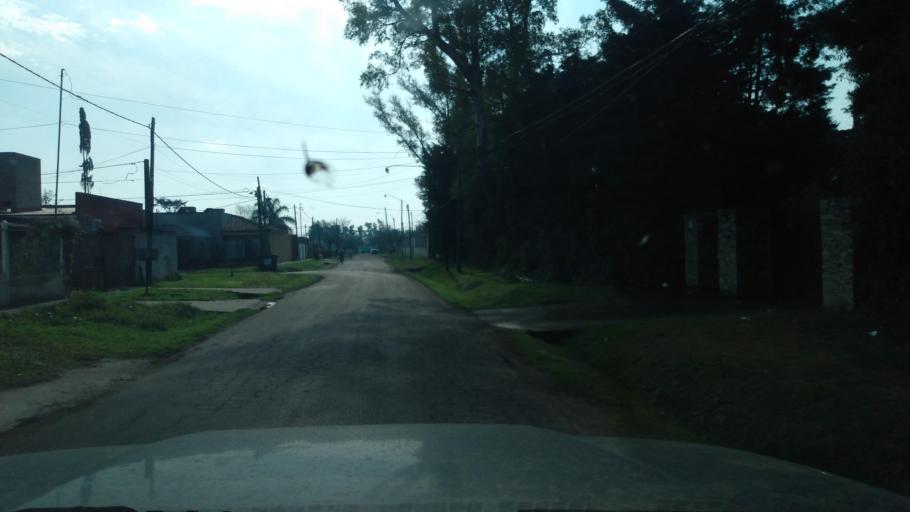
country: AR
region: Buenos Aires
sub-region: Partido de Lujan
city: Lujan
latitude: -34.5704
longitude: -59.0873
